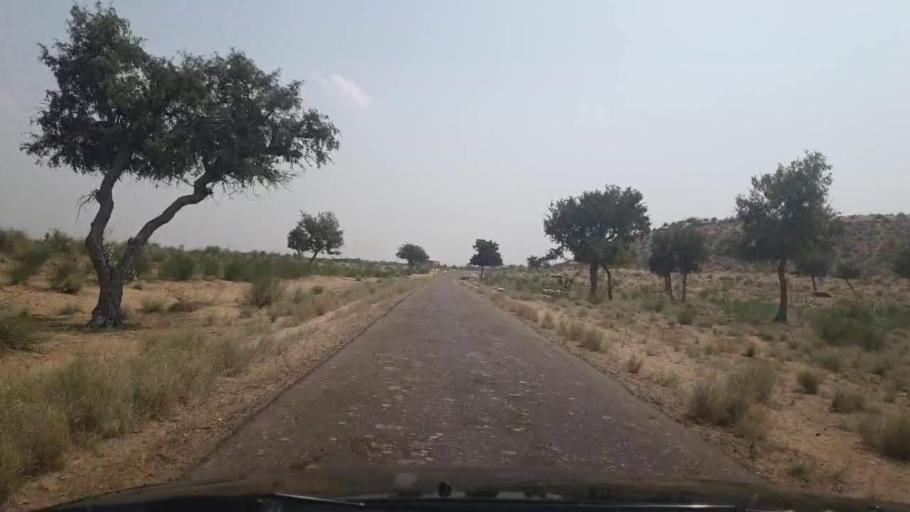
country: PK
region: Sindh
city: Islamkot
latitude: 25.0101
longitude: 70.4053
